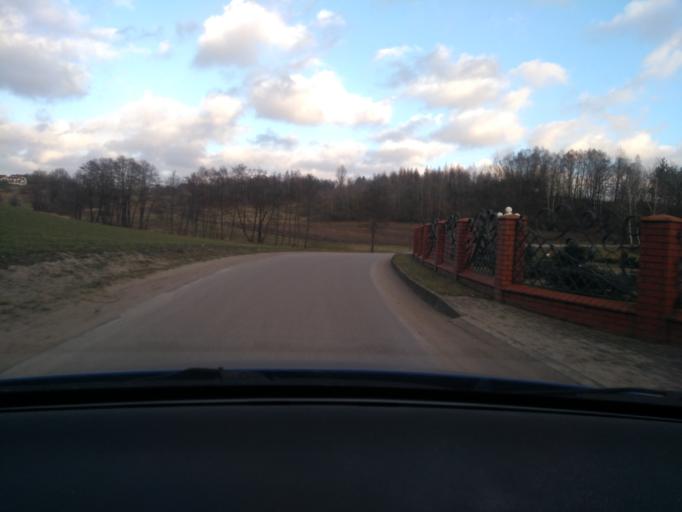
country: PL
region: Pomeranian Voivodeship
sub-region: Powiat kartuski
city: Przodkowo
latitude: 54.4152
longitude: 18.2486
